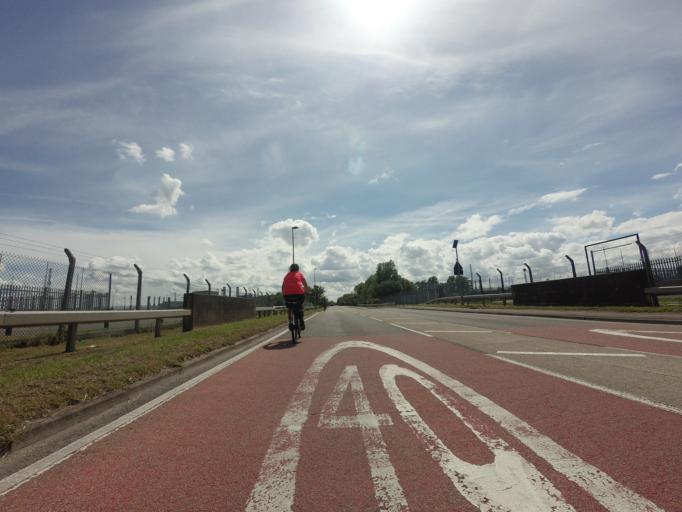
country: GB
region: England
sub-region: Medway
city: Allhallows
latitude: 51.4467
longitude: 0.6935
